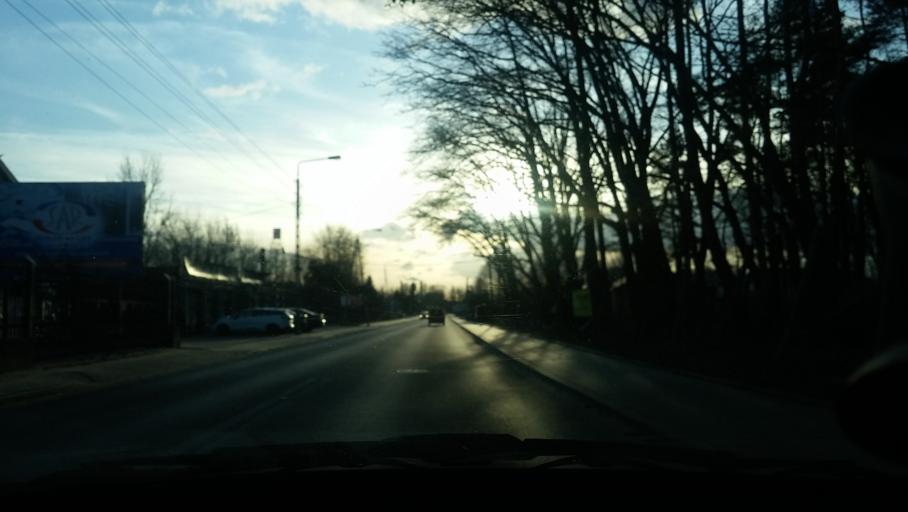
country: PL
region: Masovian Voivodeship
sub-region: Warszawa
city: Wawer
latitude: 52.2026
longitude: 21.1565
